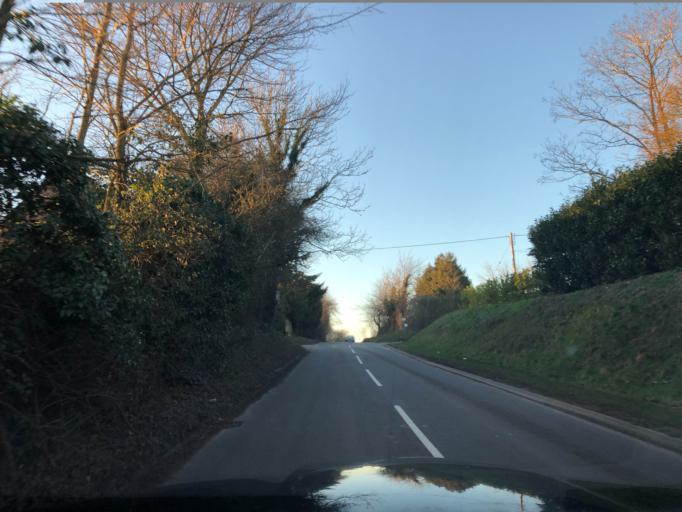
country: GB
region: England
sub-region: Warwickshire
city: Harbury
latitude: 52.2158
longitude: -1.4375
